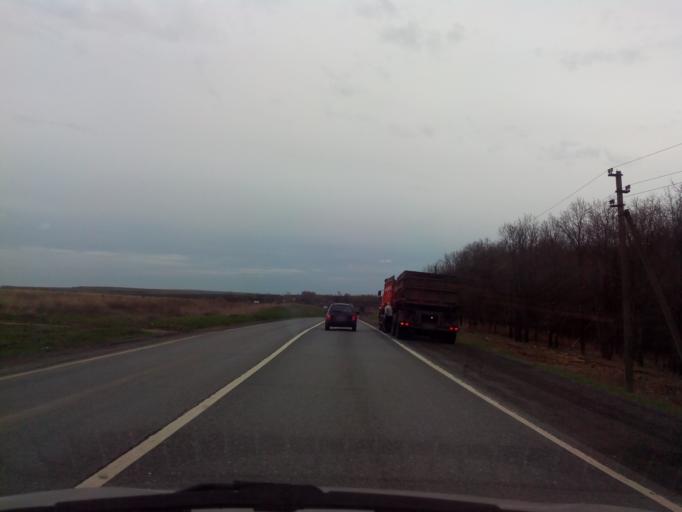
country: RU
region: Moskovskaya
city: Ozherel'ye
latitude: 54.6916
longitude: 38.3164
